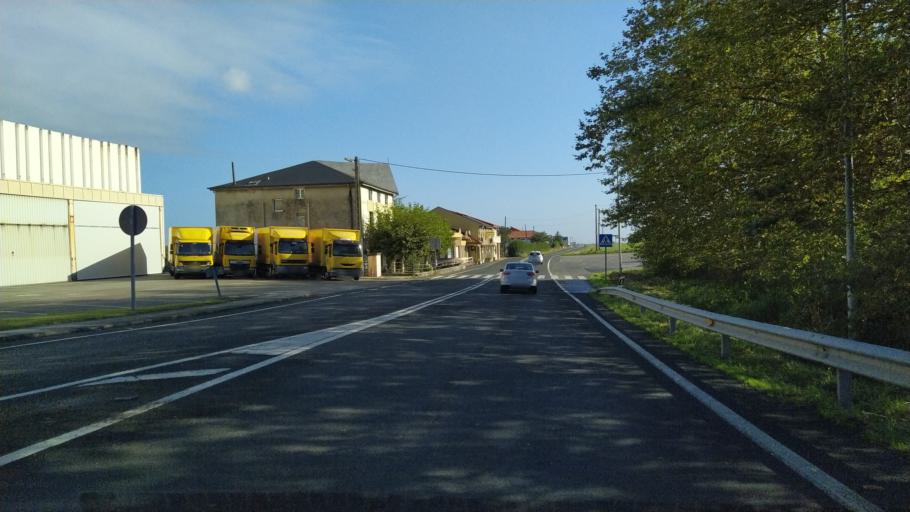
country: ES
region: Cantabria
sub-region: Provincia de Cantabria
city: Santa Cruz de Bezana
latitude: 43.4311
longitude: -3.9165
